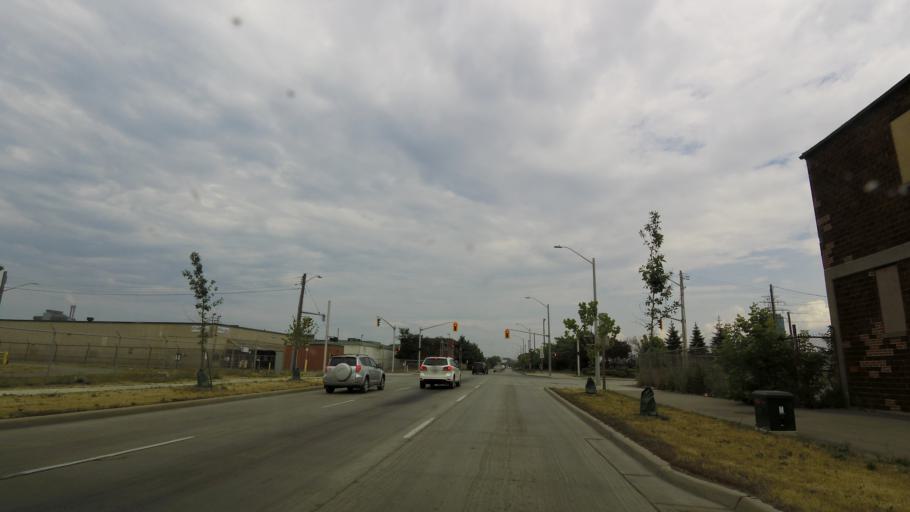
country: CA
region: Ontario
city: Hamilton
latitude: 43.2617
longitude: -79.8179
